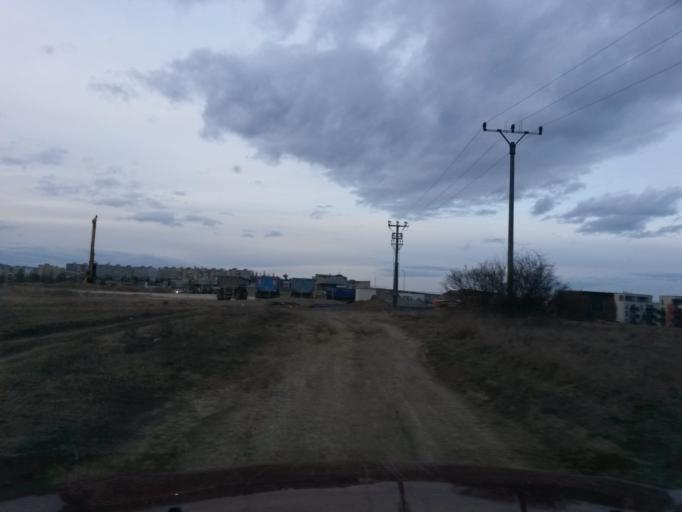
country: SK
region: Kosicky
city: Kosice
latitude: 48.7253
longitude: 21.2944
